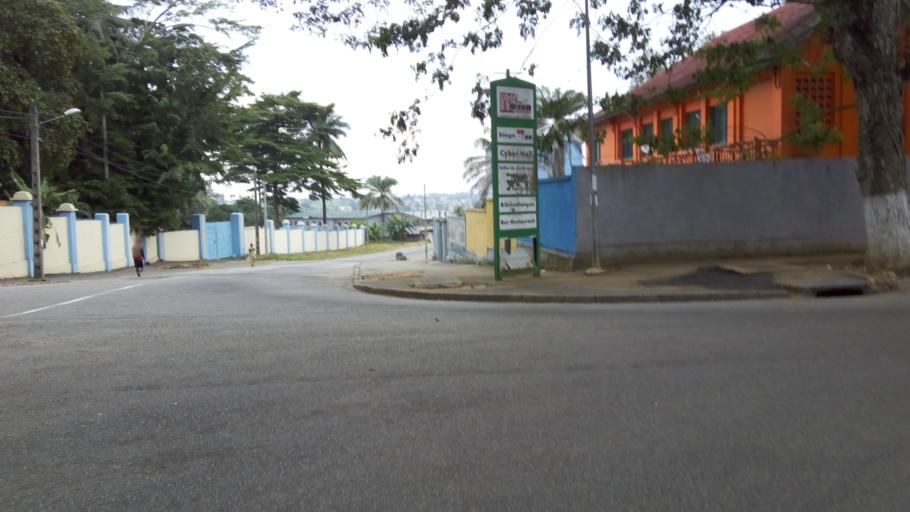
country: CI
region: Lagunes
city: Abidjan
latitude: 5.3210
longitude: -4.0217
